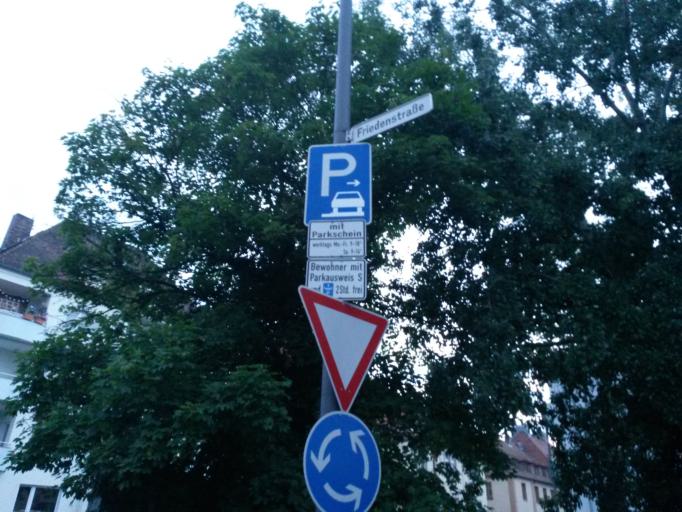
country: DE
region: Bavaria
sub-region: Regierungsbezirk Unterfranken
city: Wuerzburg
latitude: 49.7835
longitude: 9.9370
